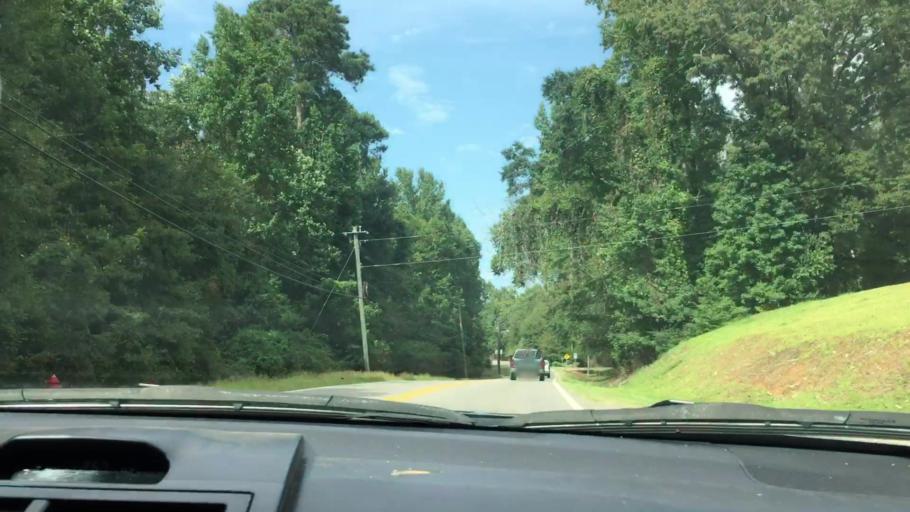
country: US
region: Alabama
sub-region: Hale County
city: Greensboro
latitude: 32.6969
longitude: -87.6028
